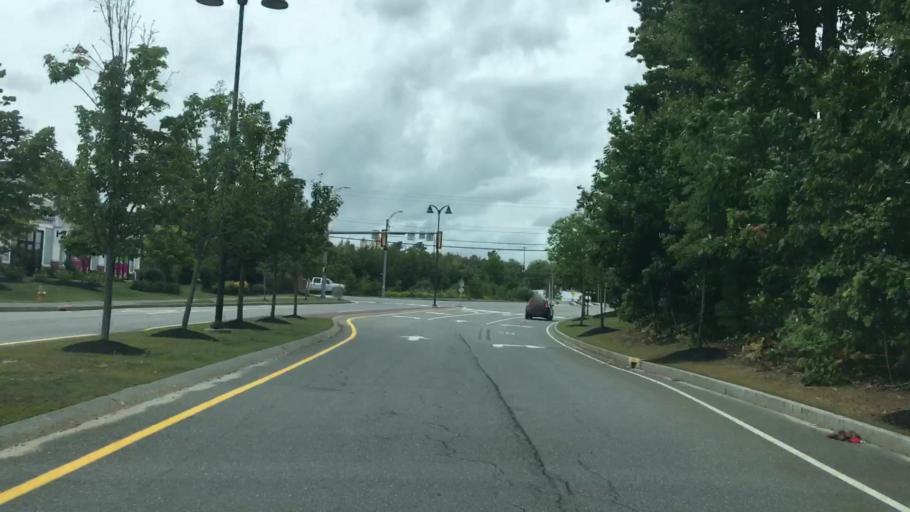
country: US
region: Maine
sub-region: Cumberland County
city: South Portland Gardens
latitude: 43.6242
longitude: -70.3453
